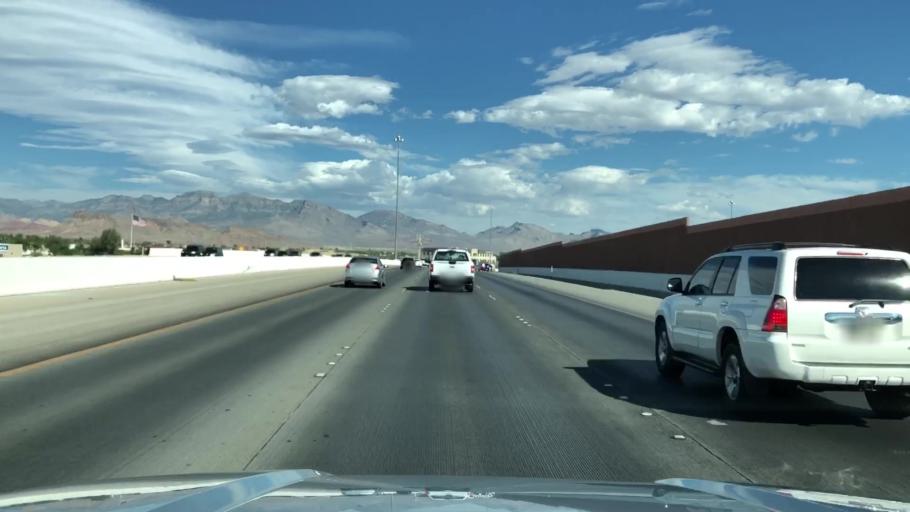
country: US
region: Nevada
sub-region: Clark County
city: Summerlin South
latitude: 36.0982
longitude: -115.2920
